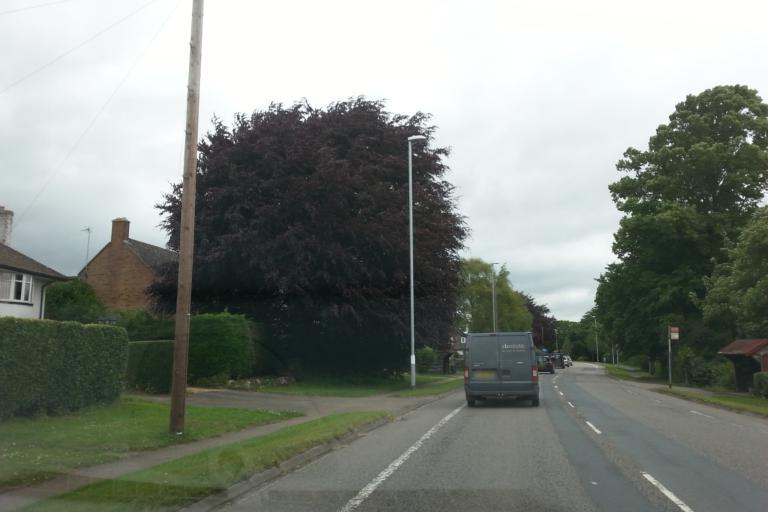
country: GB
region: England
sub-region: Cambridgeshire
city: Cambridge
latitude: 52.1576
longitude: 0.1279
